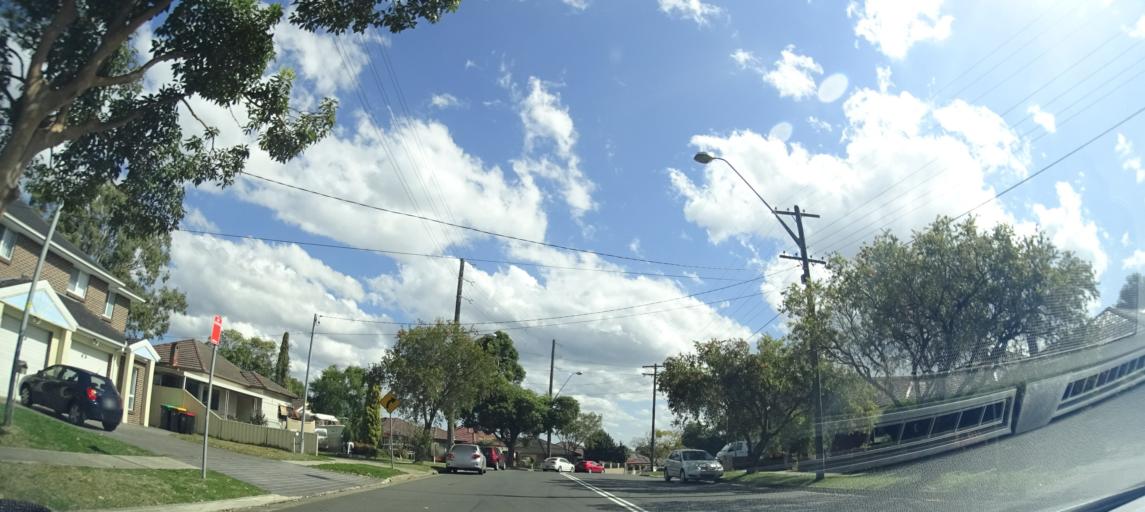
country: AU
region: New South Wales
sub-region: Bankstown
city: Padstow
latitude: -33.9512
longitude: 151.0253
